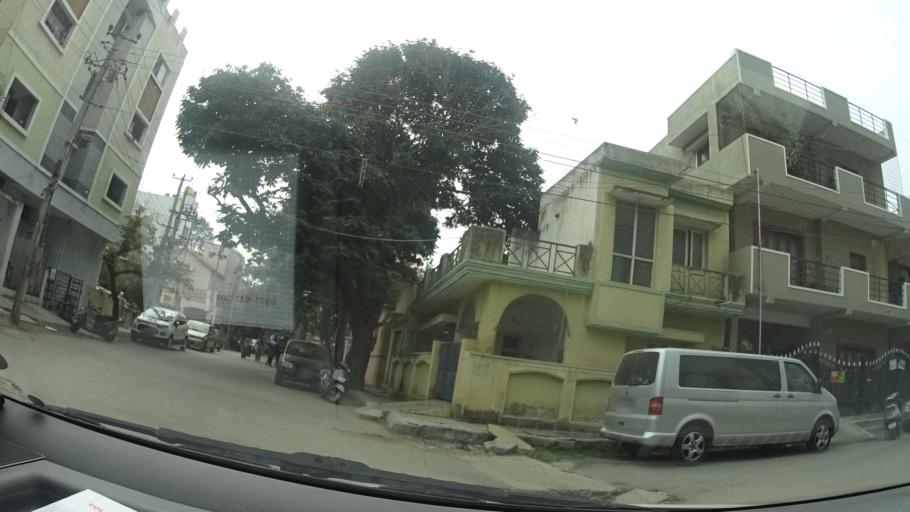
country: IN
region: Karnataka
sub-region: Bangalore Urban
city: Bangalore
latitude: 13.0235
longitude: 77.6250
